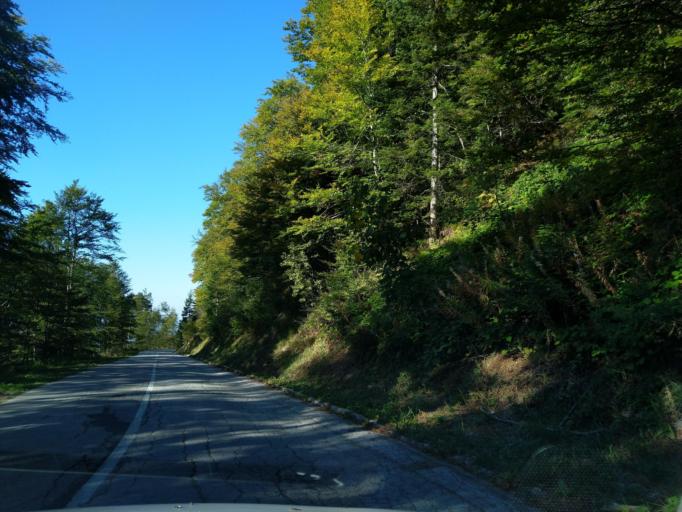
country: RS
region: Central Serbia
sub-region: Moravicki Okrug
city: Ivanjica
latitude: 43.4341
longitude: 20.2680
